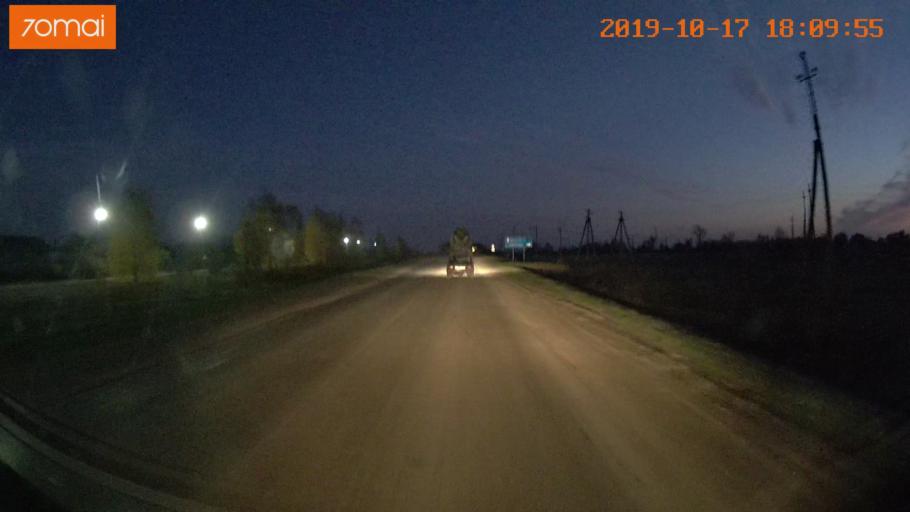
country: RU
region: Tula
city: Kurkino
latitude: 53.4216
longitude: 38.6454
